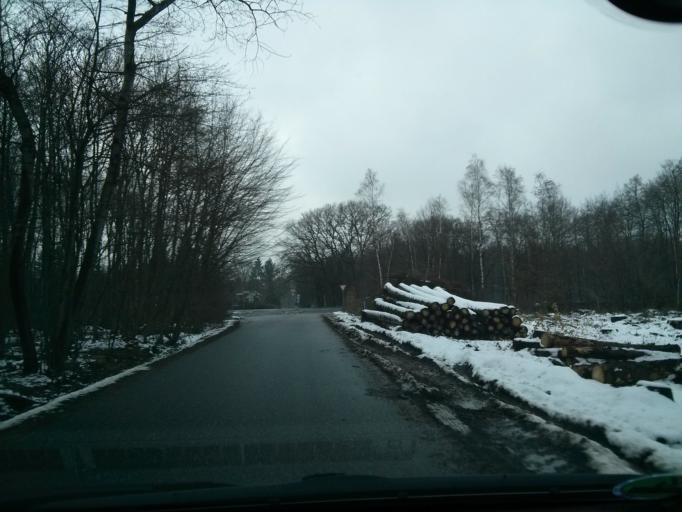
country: DE
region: North Rhine-Westphalia
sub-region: Regierungsbezirk Koln
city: Alfter
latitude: 50.6880
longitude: 6.9946
